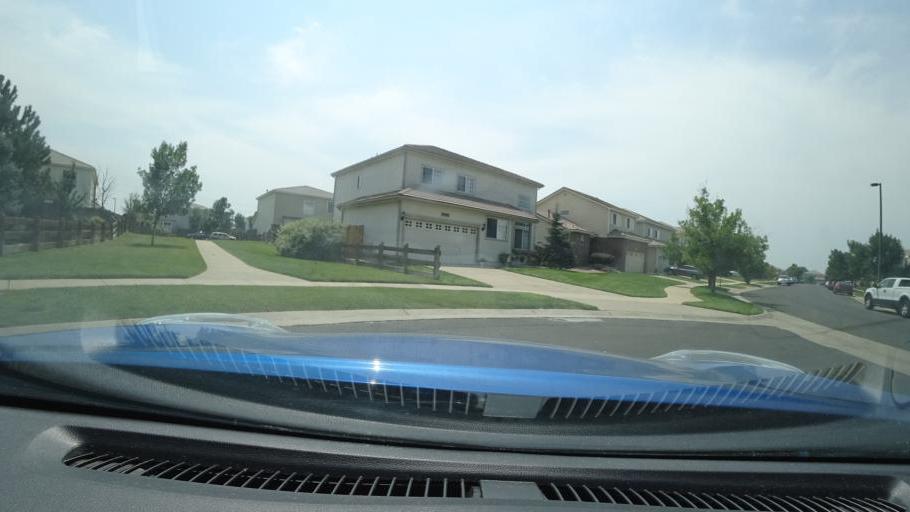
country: US
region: Colorado
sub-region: Adams County
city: Aurora
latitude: 39.7715
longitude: -104.7495
